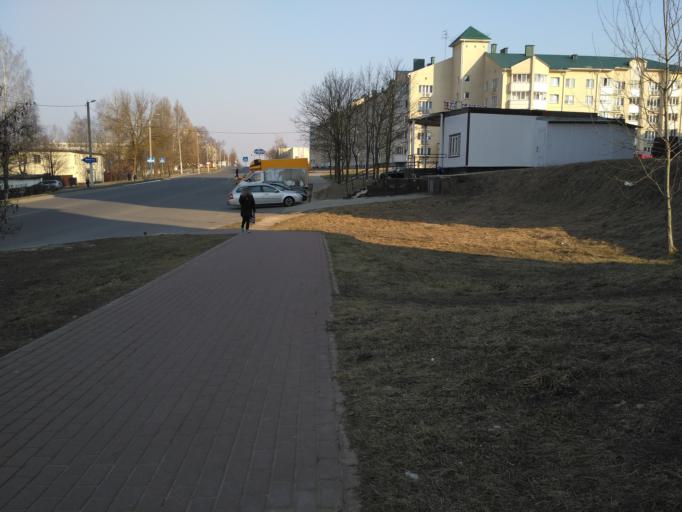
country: BY
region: Minsk
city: Zaslawye
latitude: 54.0134
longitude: 27.2602
